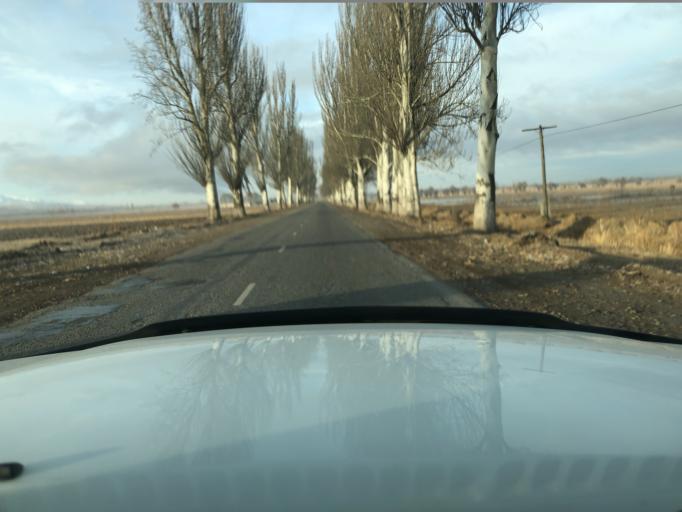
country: KG
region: Ysyk-Koel
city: Karakol
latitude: 42.4778
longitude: 78.3347
